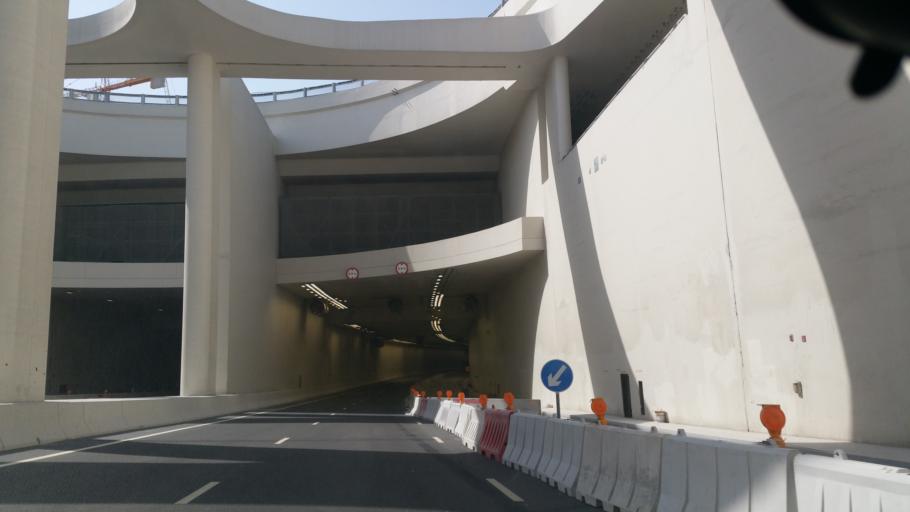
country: QA
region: Baladiyat Umm Salal
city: Umm Salal Muhammad
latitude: 25.4149
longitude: 51.5072
